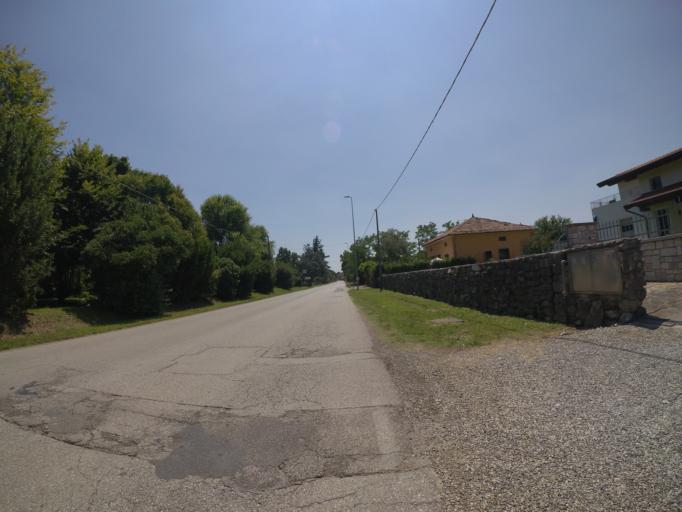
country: IT
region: Friuli Venezia Giulia
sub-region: Provincia di Udine
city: Lestizza
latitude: 45.9822
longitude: 13.1357
